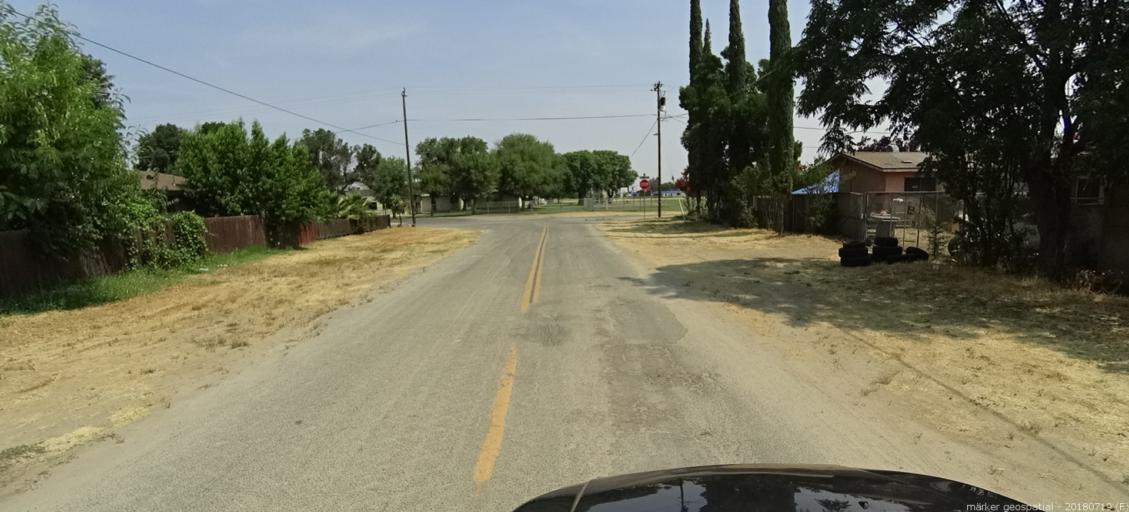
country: US
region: California
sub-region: Madera County
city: Fairmead
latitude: 37.0797
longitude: -120.1944
